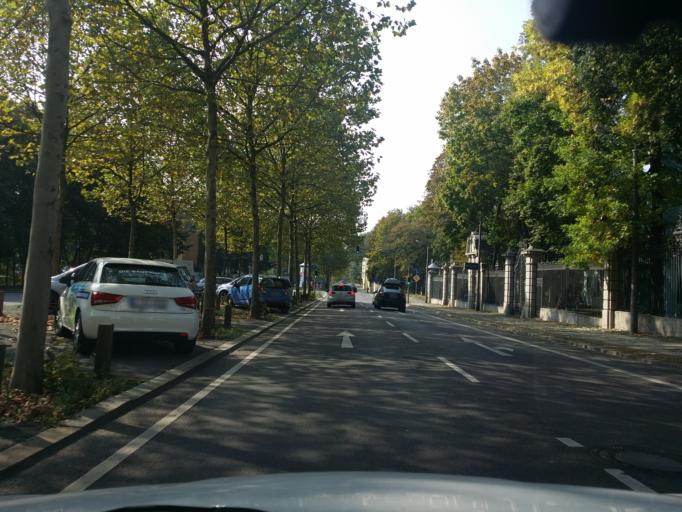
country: DE
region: Saxony
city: Leipzig
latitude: 51.3148
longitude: 12.3696
